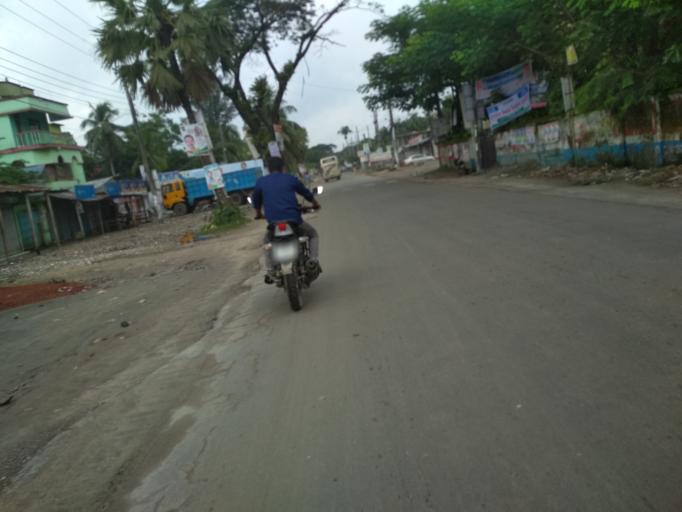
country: BD
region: Chittagong
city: Lakshmipur
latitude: 22.9451
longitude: 90.8254
